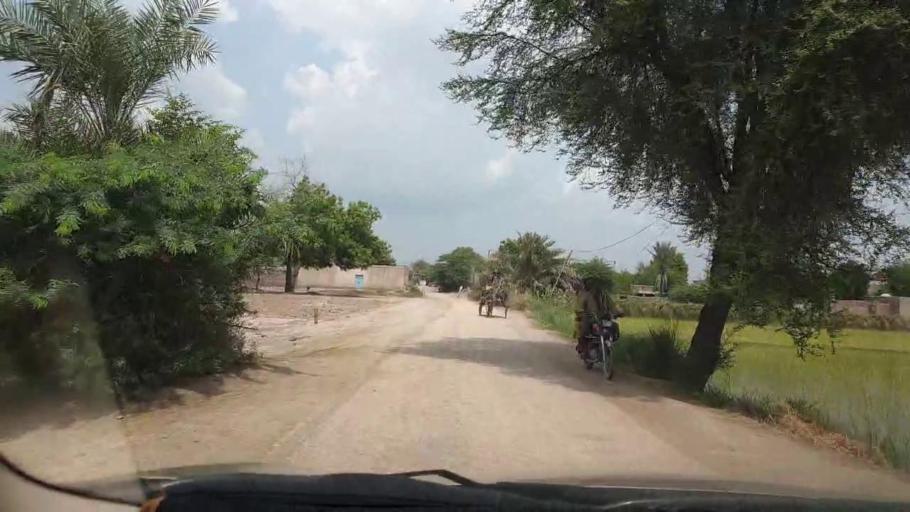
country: PK
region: Sindh
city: Larkana
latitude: 27.5761
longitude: 68.1219
